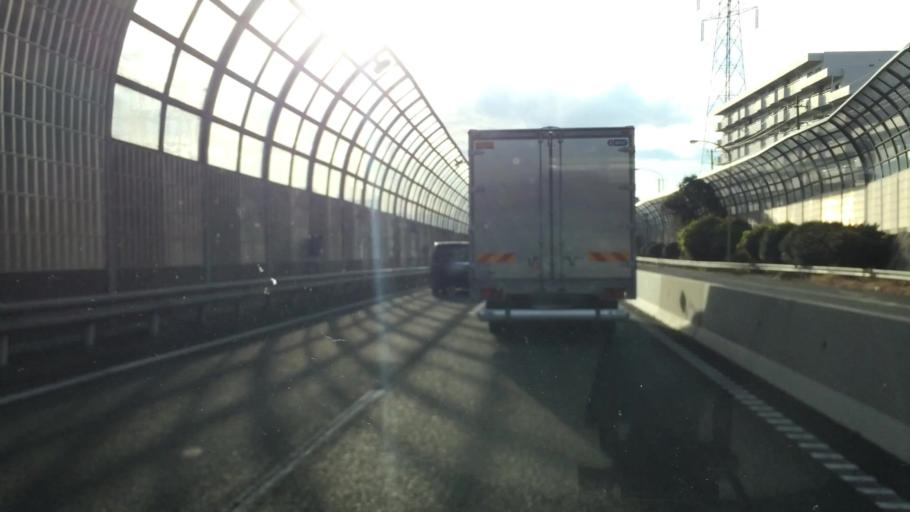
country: JP
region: Kanagawa
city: Yokohama
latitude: 35.4270
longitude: 139.5439
